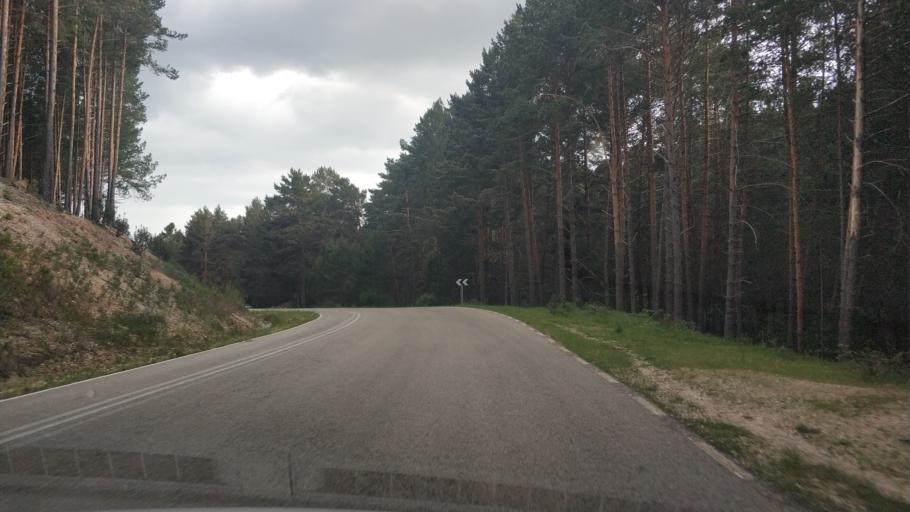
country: ES
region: Castille and Leon
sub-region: Provincia de Soria
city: San Leonardo de Yague
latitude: 41.8450
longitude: -3.0682
